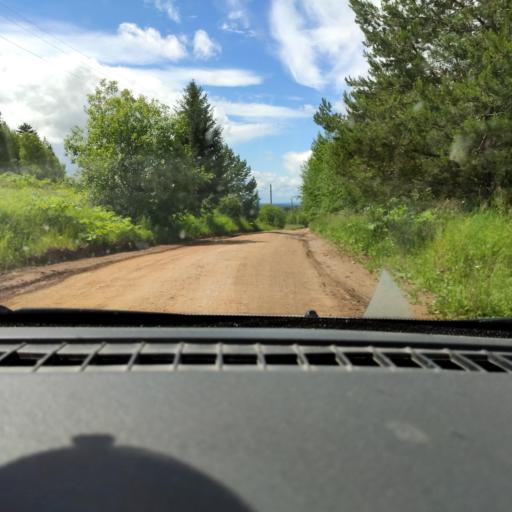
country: RU
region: Perm
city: Overyata
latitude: 58.1291
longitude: 55.8249
